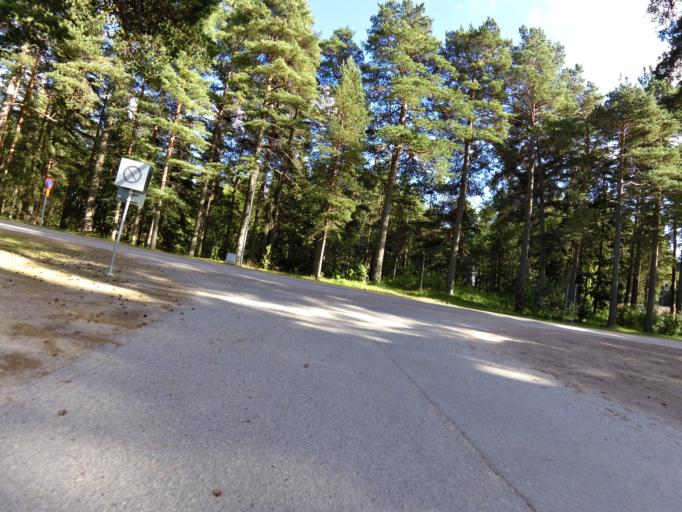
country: SE
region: Gaevleborg
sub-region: Gavle Kommun
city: Gavle
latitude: 60.7075
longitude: 17.1651
